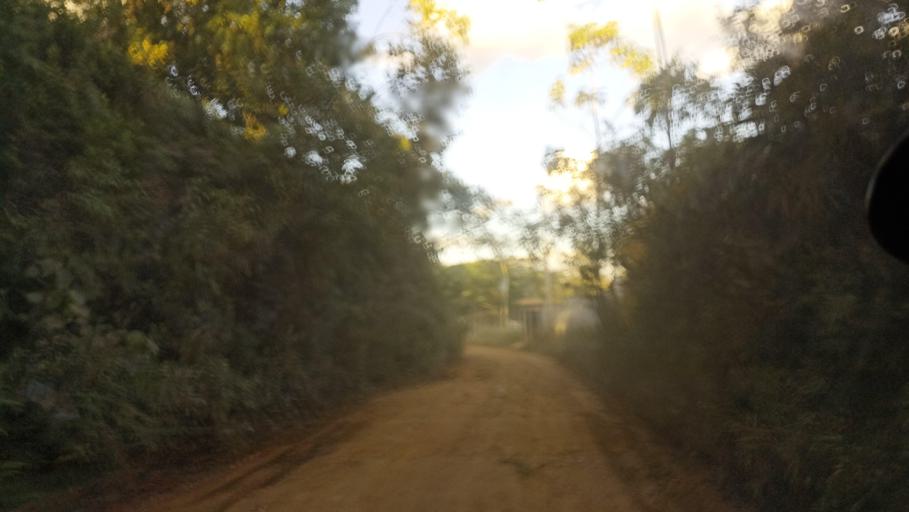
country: BR
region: Minas Gerais
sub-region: Sao Joao Del Rei
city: Sao Joao del Rei
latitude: -21.1825
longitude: -44.3447
